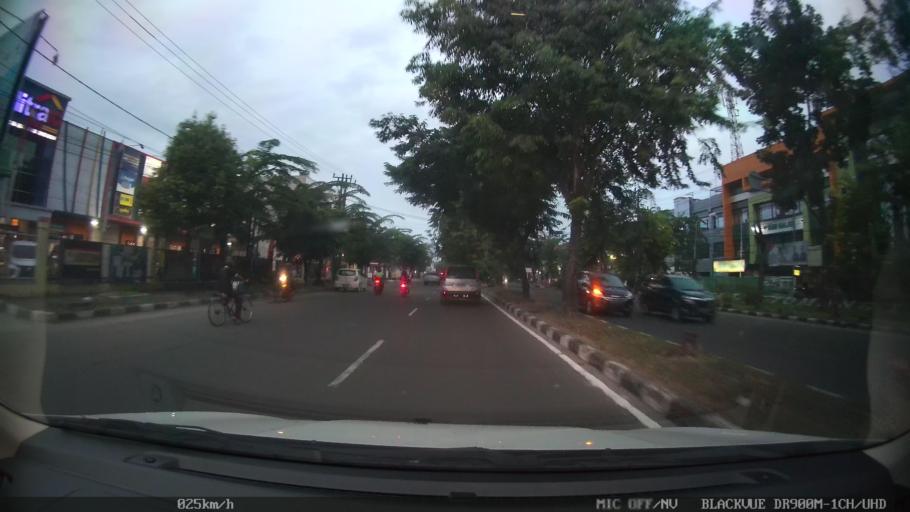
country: ID
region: North Sumatra
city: Medan
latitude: 3.5910
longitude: 98.6401
